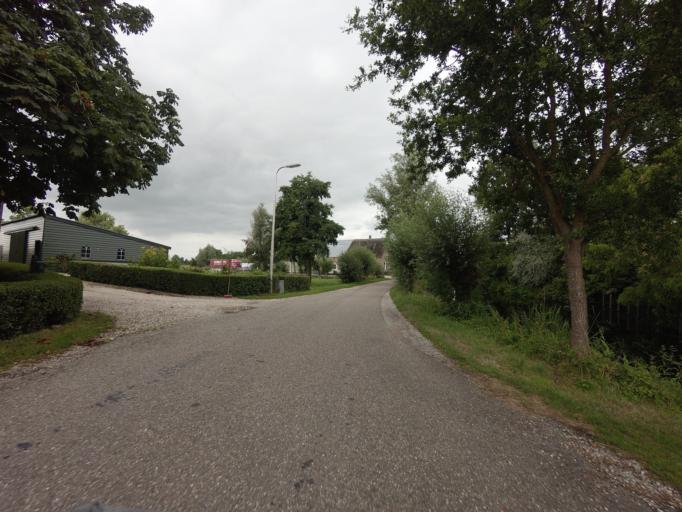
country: NL
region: South Holland
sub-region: Gemeente Giessenlanden
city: Giessenburg
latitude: 51.9040
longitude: 4.9041
